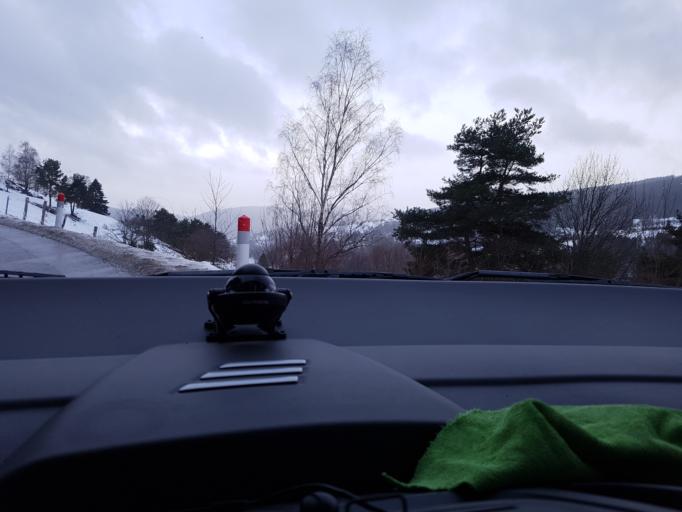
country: FR
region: Alsace
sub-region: Departement du Haut-Rhin
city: Soultzeren
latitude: 48.0802
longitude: 7.1062
